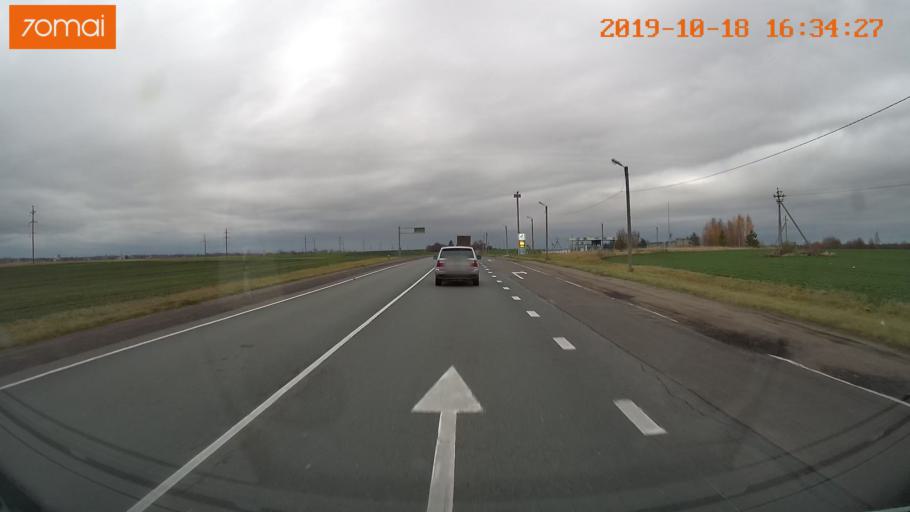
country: RU
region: Vladimir
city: Suzdal'
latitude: 56.3896
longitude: 40.4594
